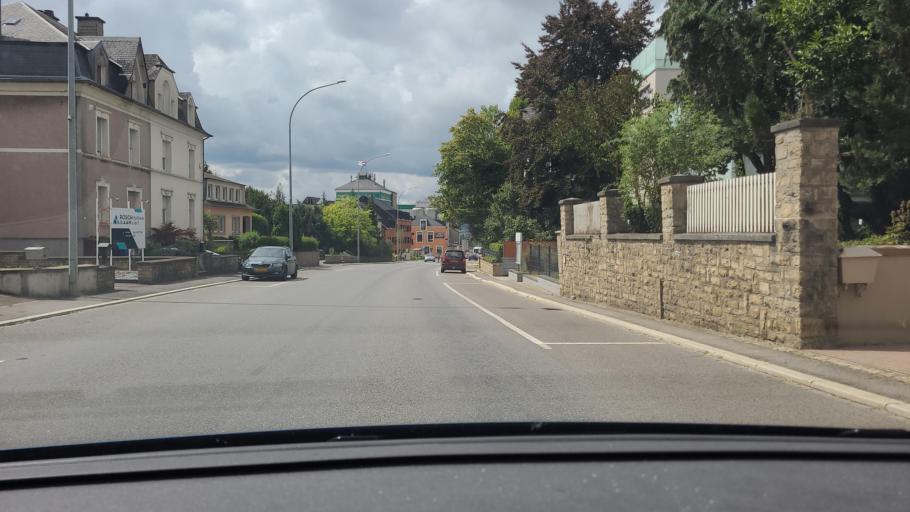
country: LU
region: Luxembourg
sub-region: Canton de Capellen
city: Bascharage
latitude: 49.5690
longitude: 5.9145
